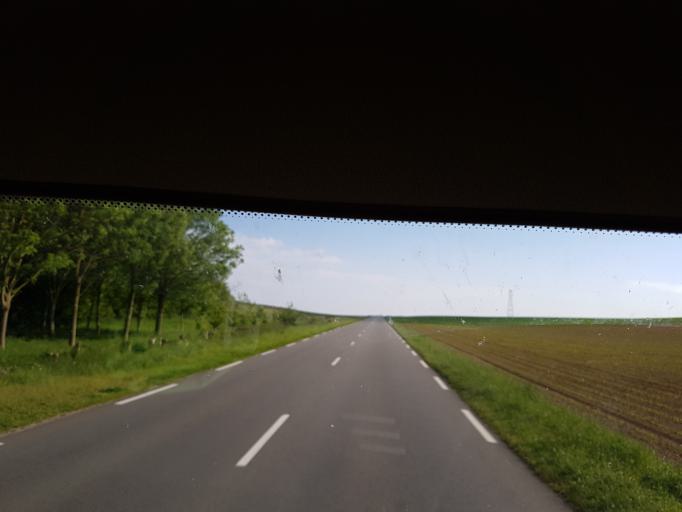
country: FR
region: Picardie
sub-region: Departement de la Somme
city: Crecy-en-Ponthieu
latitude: 50.2521
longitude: 1.9651
